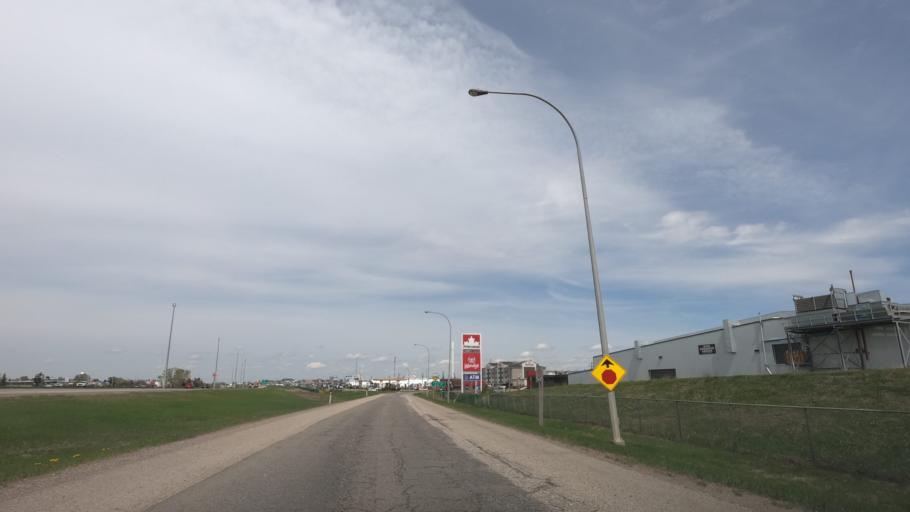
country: CA
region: Alberta
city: Airdrie
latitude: 51.2847
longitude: -114.0004
